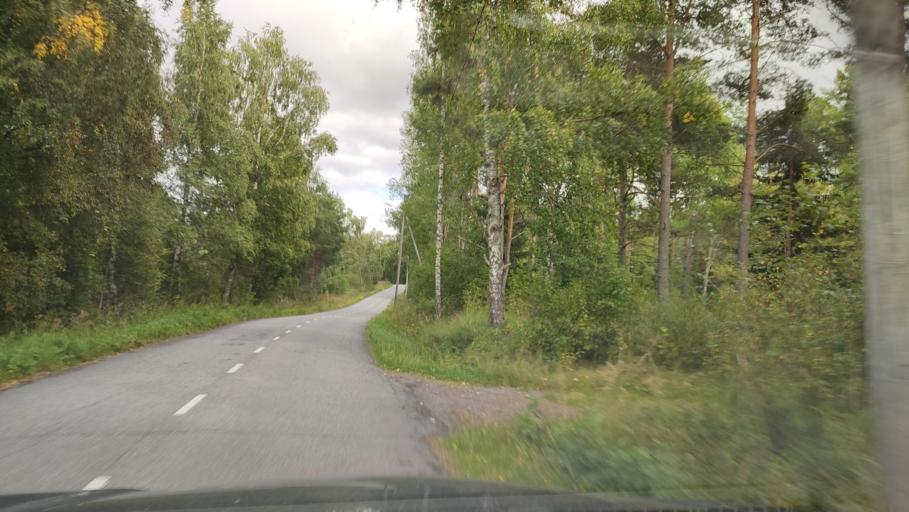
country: FI
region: Ostrobothnia
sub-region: Sydosterbotten
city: Kristinestad
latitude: 62.2752
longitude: 21.3581
